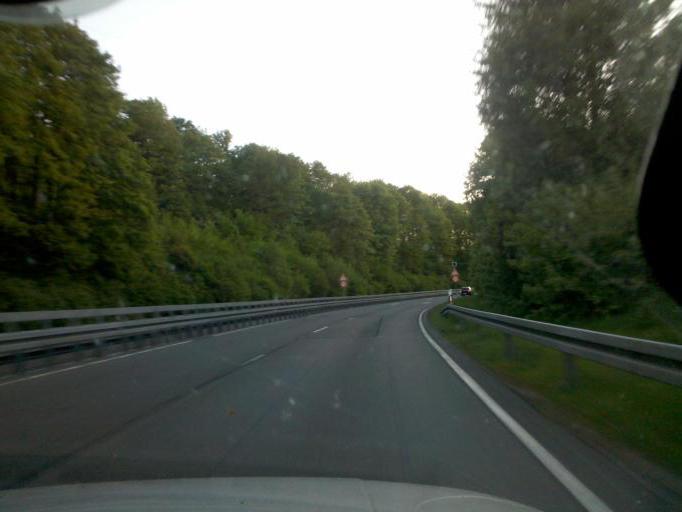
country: DE
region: North Rhine-Westphalia
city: Wiehl
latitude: 50.9761
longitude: 7.5416
